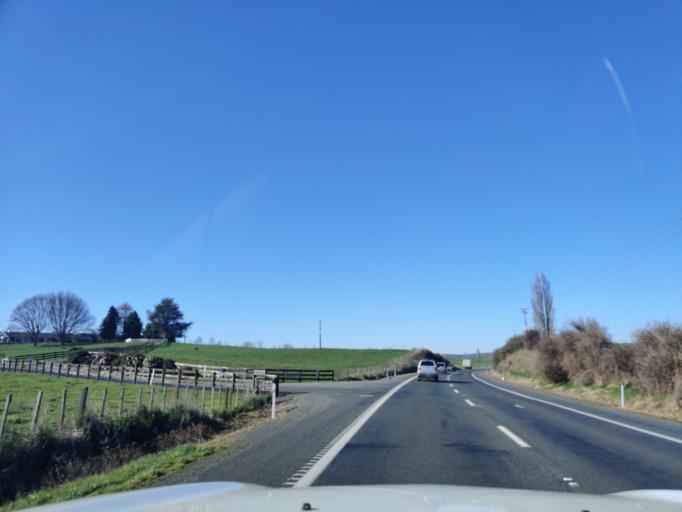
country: NZ
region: Waikato
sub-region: Matamata-Piako District
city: Matamata
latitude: -38.0265
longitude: 175.7885
